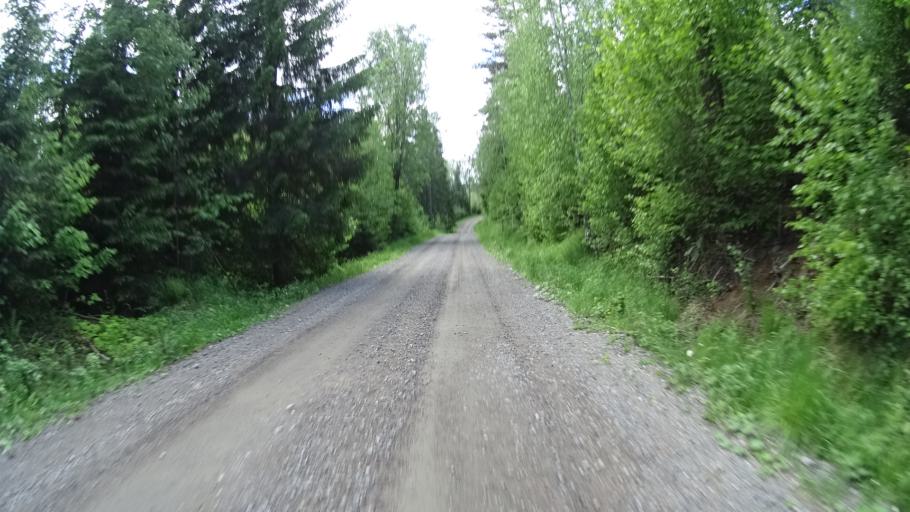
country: FI
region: Uusimaa
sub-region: Raaseporin
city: Karis
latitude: 60.1603
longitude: 23.6091
